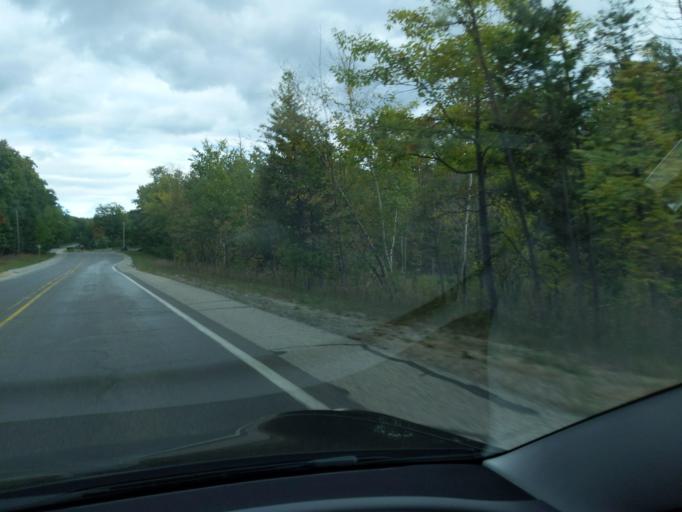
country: US
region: Michigan
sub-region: Kalkaska County
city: Rapid City
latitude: 44.7826
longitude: -85.2747
